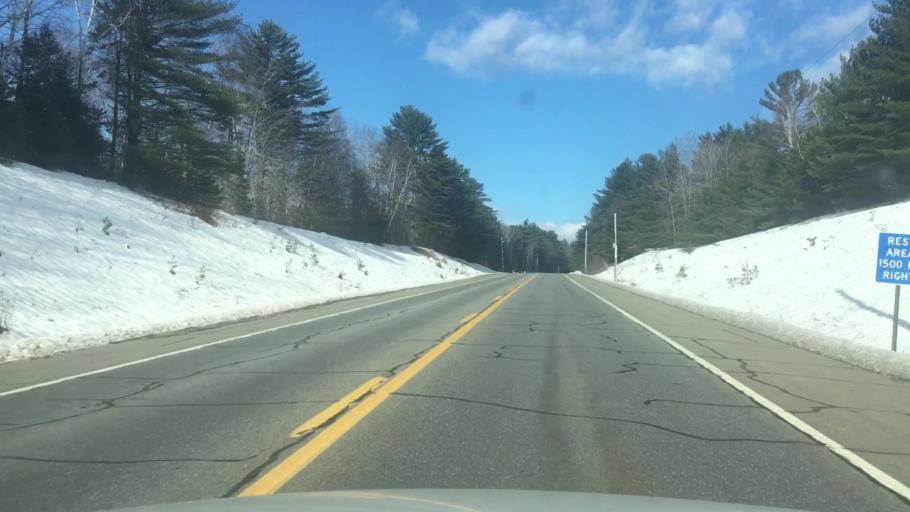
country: US
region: Maine
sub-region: Somerset County
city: Madison
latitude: 44.9778
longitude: -69.8664
